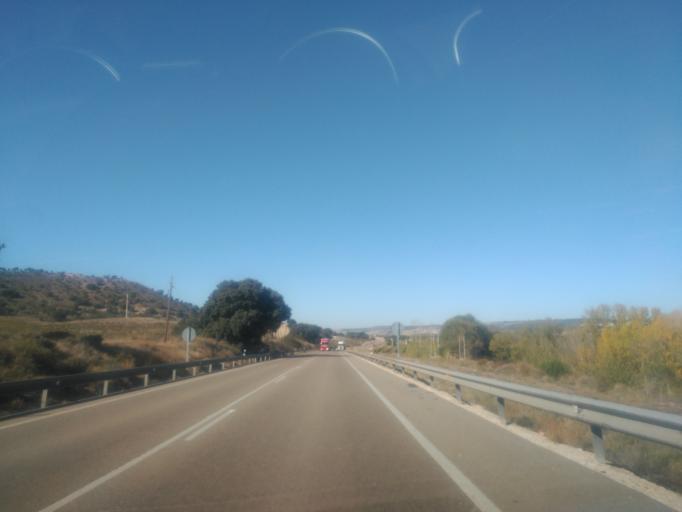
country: ES
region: Castille and Leon
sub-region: Provincia de Valladolid
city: Valbuena de Duero
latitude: 41.6249
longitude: -4.2736
